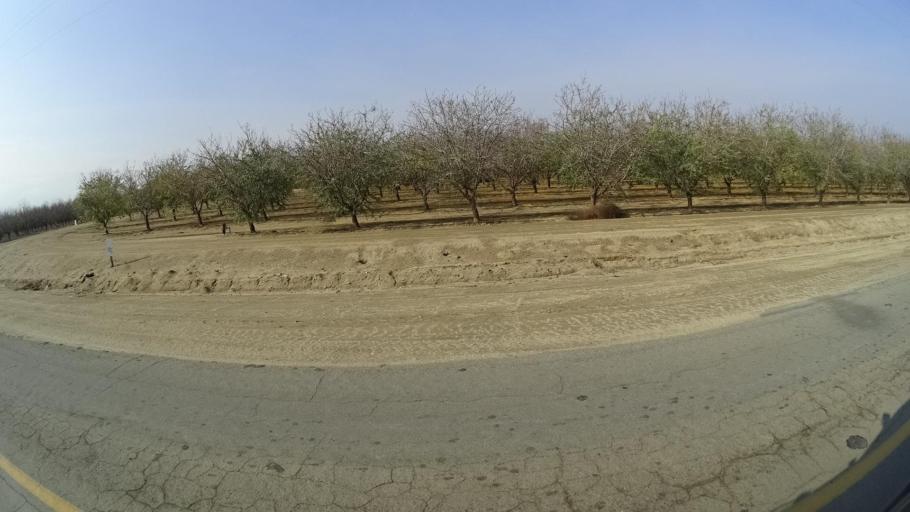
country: US
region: California
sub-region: Kern County
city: Lebec
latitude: 34.9934
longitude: -118.8466
